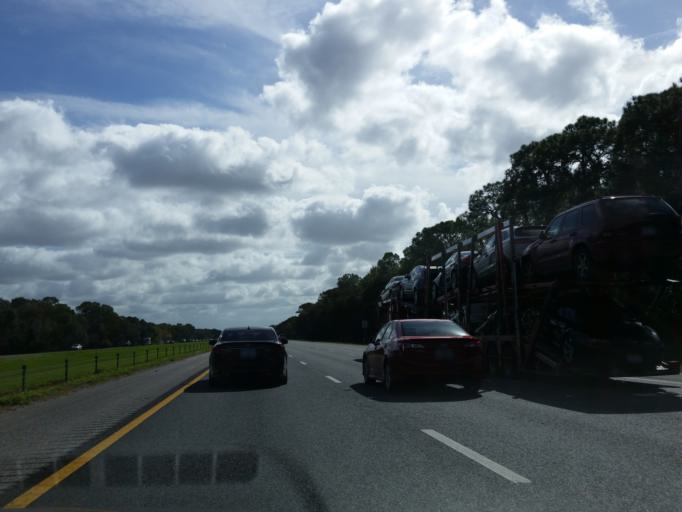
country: US
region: Florida
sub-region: Manatee County
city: Ellenton
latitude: 27.4823
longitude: -82.4681
